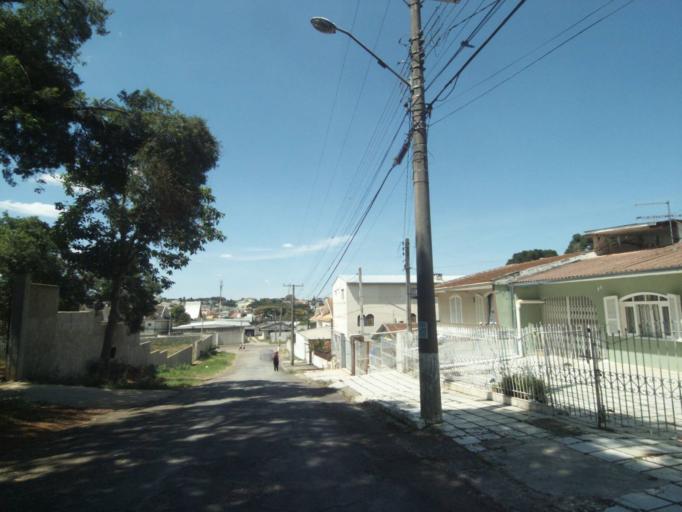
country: BR
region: Parana
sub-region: Curitiba
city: Curitiba
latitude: -25.4657
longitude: -49.2469
